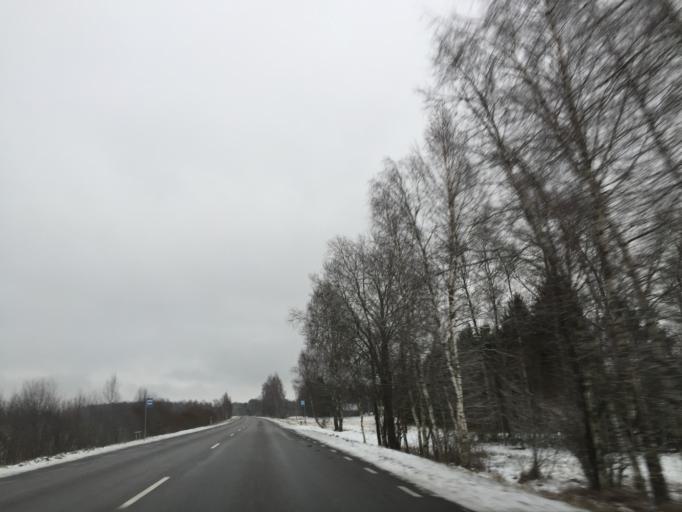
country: EE
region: Laeaene
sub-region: Lihula vald
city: Lihula
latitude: 58.6351
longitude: 23.8650
